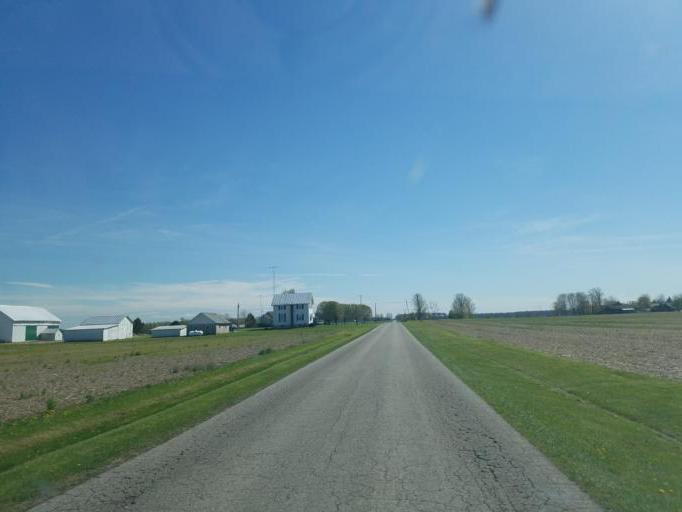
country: US
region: Ohio
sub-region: Huron County
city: Bellevue
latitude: 41.1939
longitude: -82.8798
